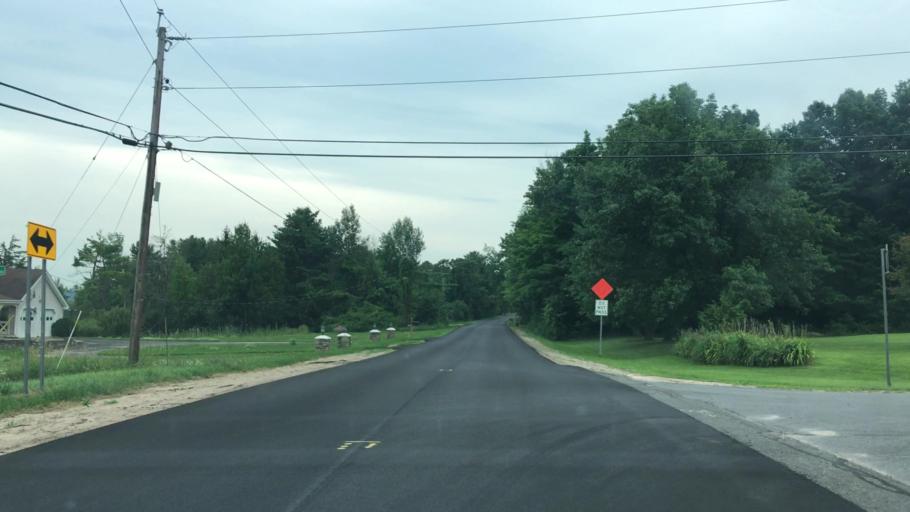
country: US
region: New York
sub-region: Clinton County
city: Peru
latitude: 44.5633
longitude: -73.5682
